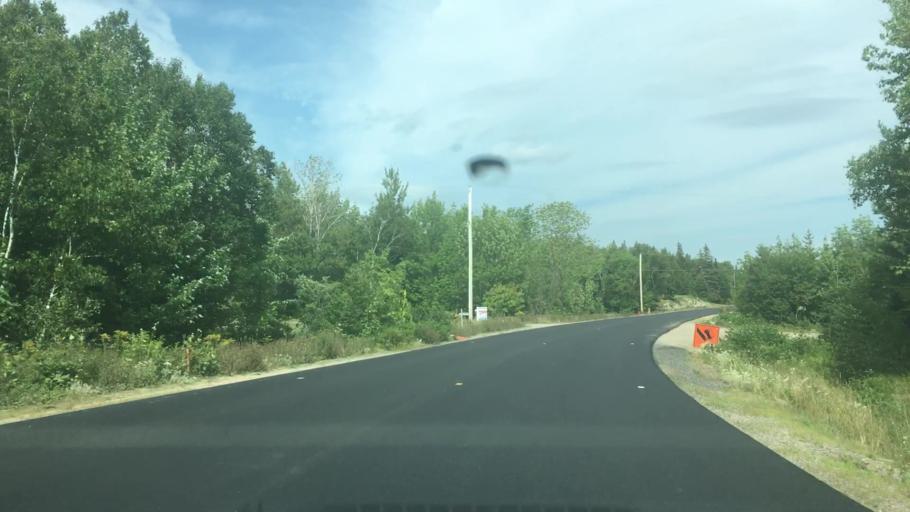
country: CA
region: Nova Scotia
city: Sydney Mines
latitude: 46.5499
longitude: -60.4116
